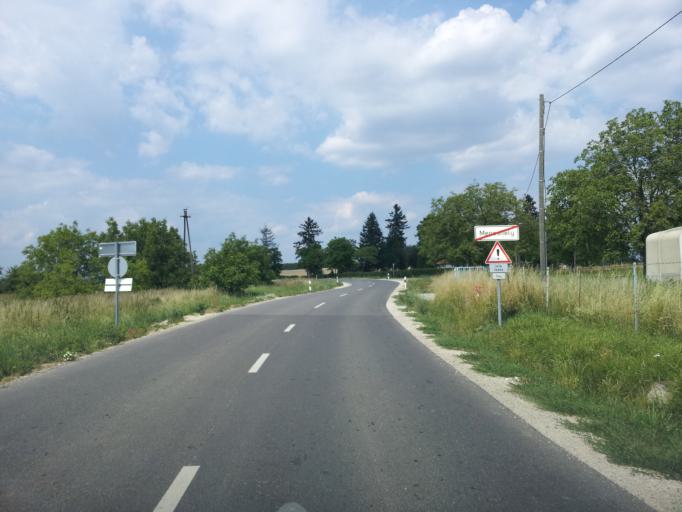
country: HU
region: Veszprem
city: Zanka
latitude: 46.9484
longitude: 17.7013
